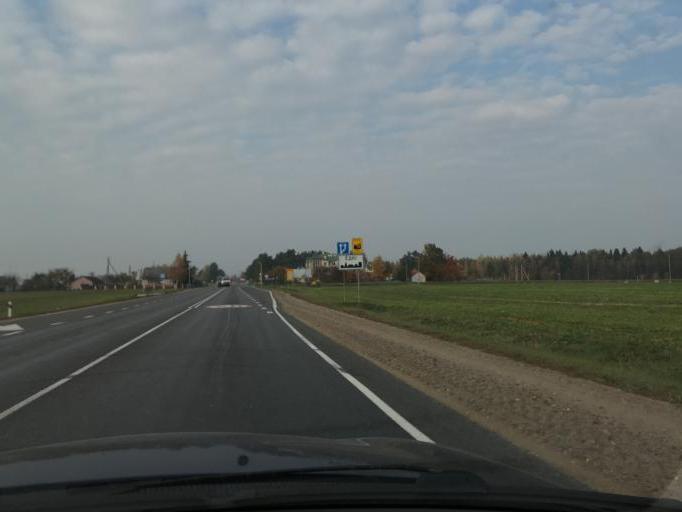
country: BY
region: Grodnenskaya
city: Lida
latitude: 53.8473
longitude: 25.3409
